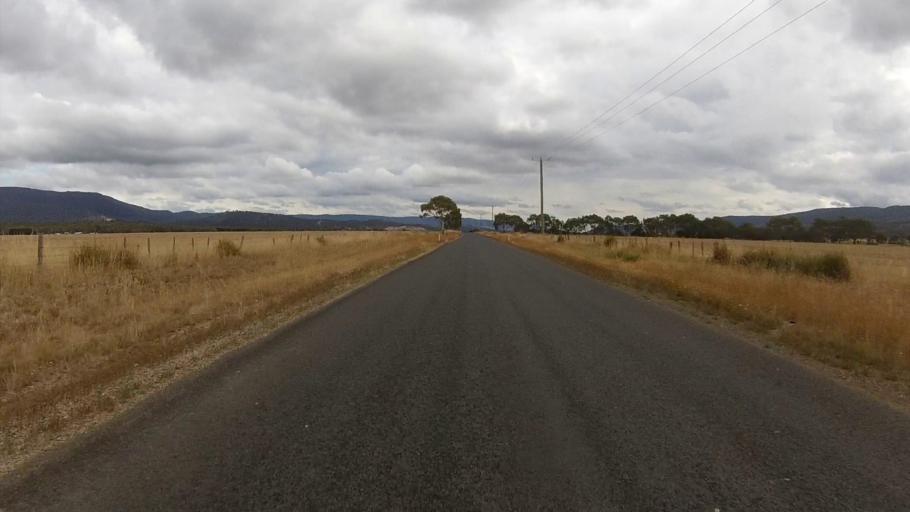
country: AU
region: Tasmania
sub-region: Break O'Day
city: St Helens
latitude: -41.8218
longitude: 147.8821
